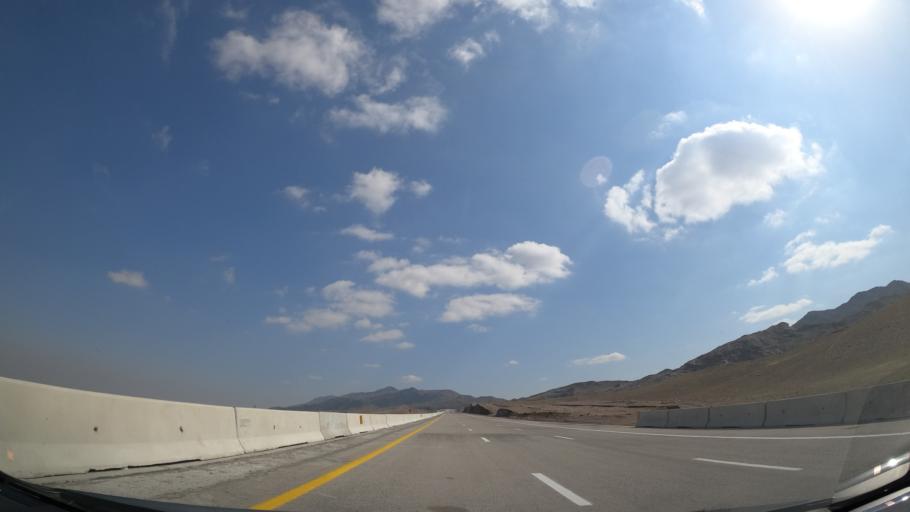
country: IR
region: Alborz
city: Nazarabad
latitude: 35.7012
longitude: 50.6196
